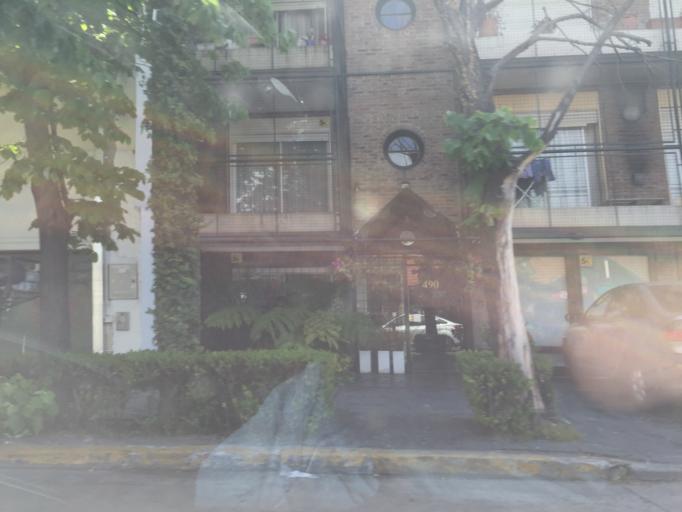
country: AR
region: Buenos Aires
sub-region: Partido de Lomas de Zamora
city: Lomas de Zamora
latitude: -34.7544
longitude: -58.4029
